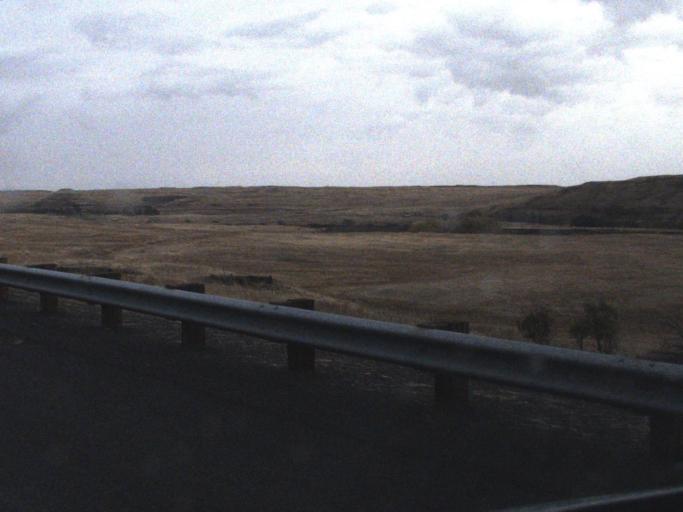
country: US
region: Washington
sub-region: Adams County
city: Ritzville
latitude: 46.7551
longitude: -118.1793
